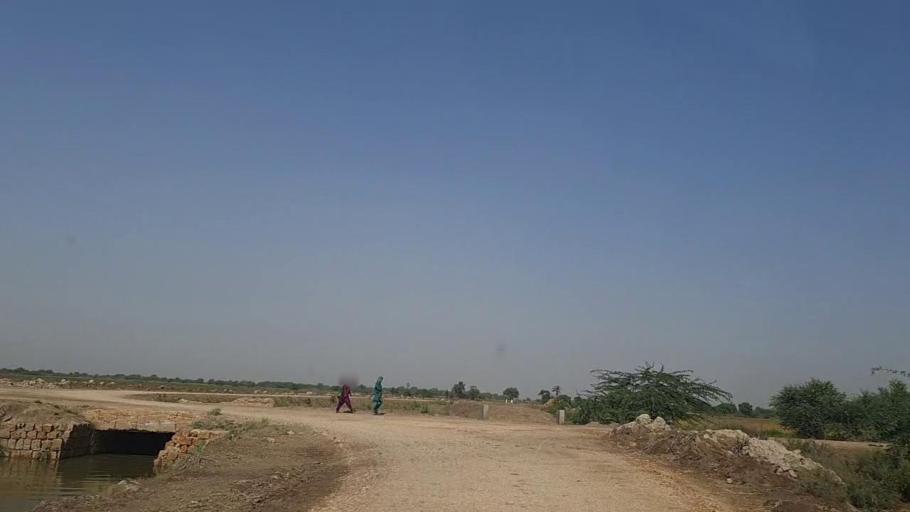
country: PK
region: Sindh
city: Daro Mehar
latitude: 24.7546
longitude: 68.1362
